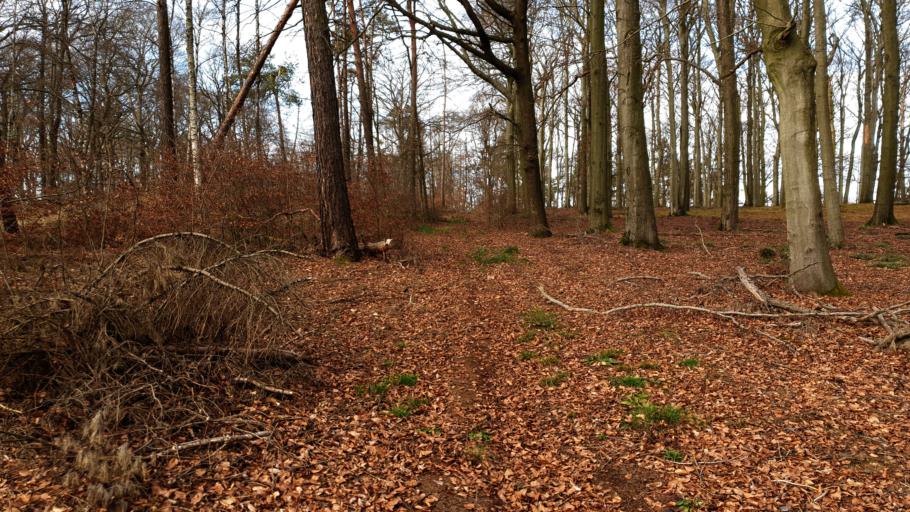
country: DE
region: Saxony
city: Hohburg
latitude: 51.4194
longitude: 12.7981
